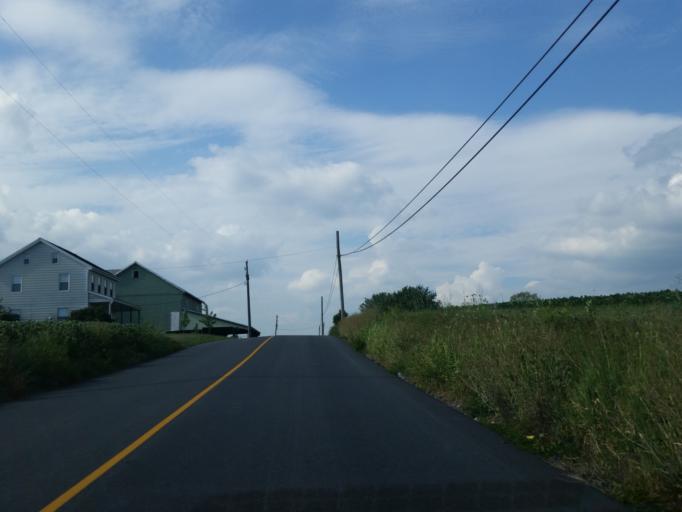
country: US
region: Pennsylvania
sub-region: Lancaster County
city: Mount Joy
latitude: 40.1461
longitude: -76.4645
